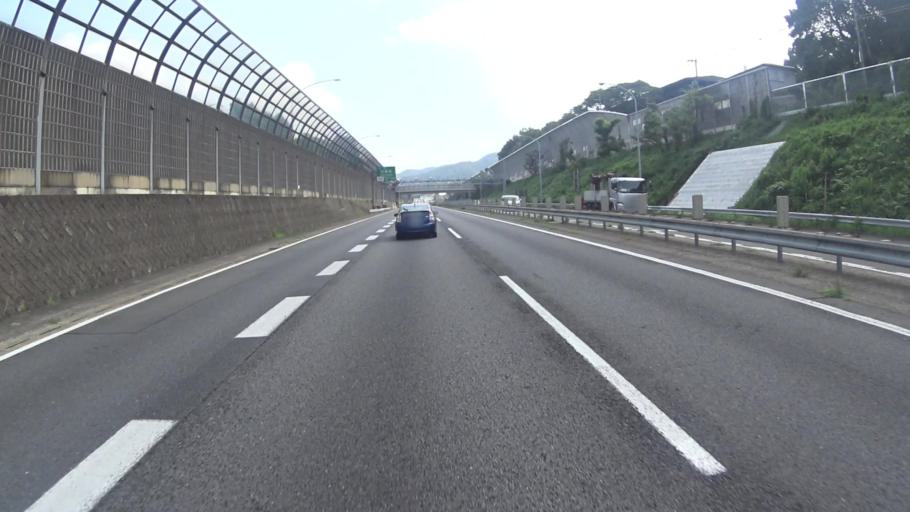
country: JP
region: Shiga Prefecture
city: Otsu-shi
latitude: 34.9780
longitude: 135.8294
